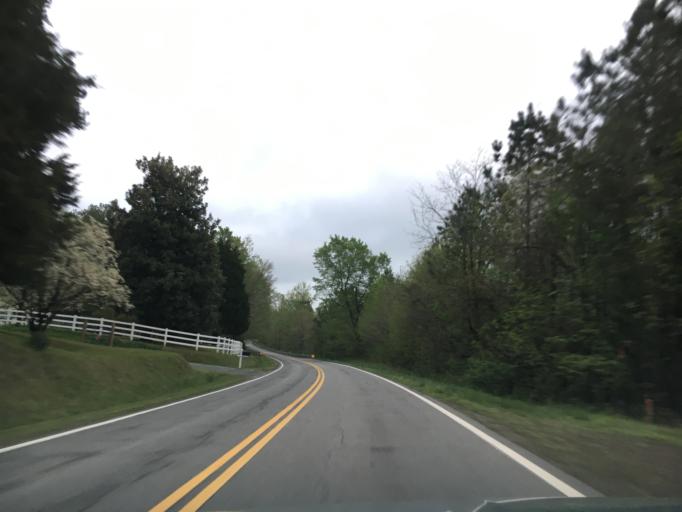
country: US
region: Virginia
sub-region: Halifax County
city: South Boston
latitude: 36.6791
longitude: -78.8940
